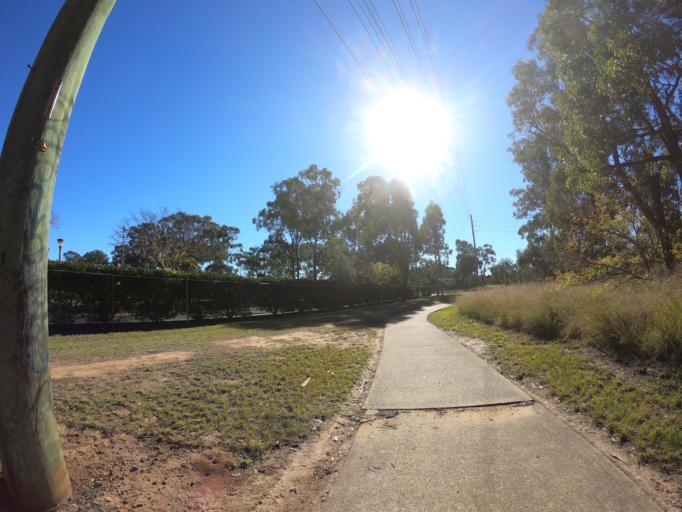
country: AU
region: New South Wales
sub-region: Hawkesbury
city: South Windsor
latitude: -33.6321
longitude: 150.7950
